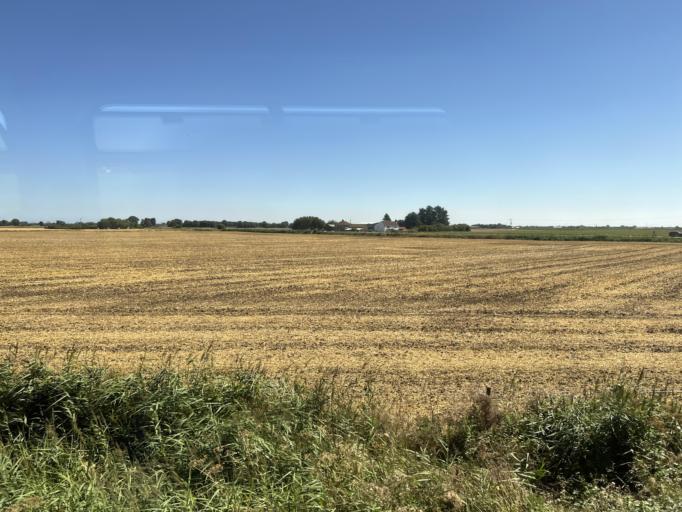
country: GB
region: England
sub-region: Lincolnshire
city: Spilsby
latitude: 53.0924
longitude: 0.1004
